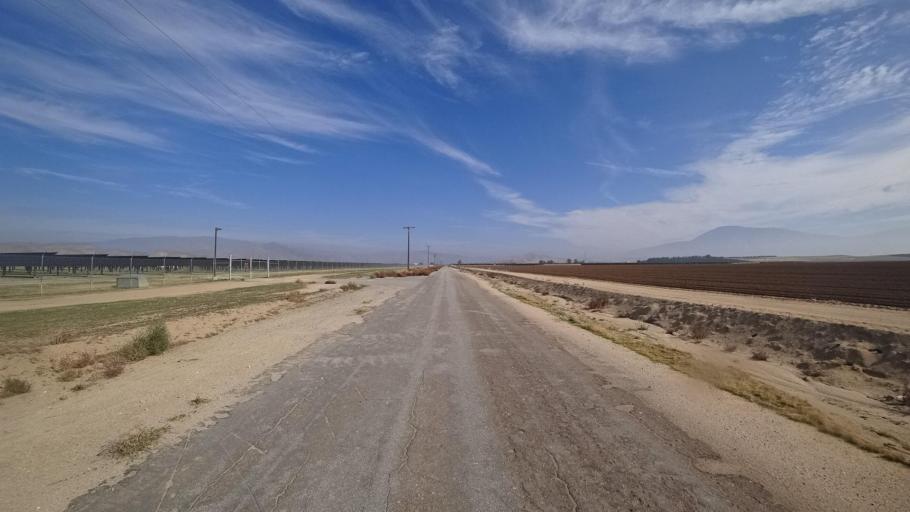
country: US
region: California
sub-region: Kern County
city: Arvin
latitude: 35.3257
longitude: -118.8072
